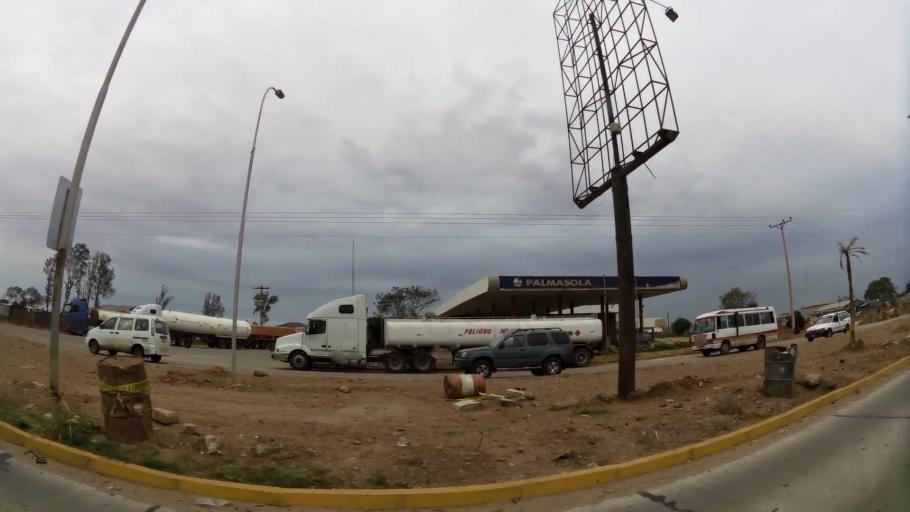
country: BO
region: Santa Cruz
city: Santa Cruz de la Sierra
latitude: -17.8499
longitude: -63.1829
